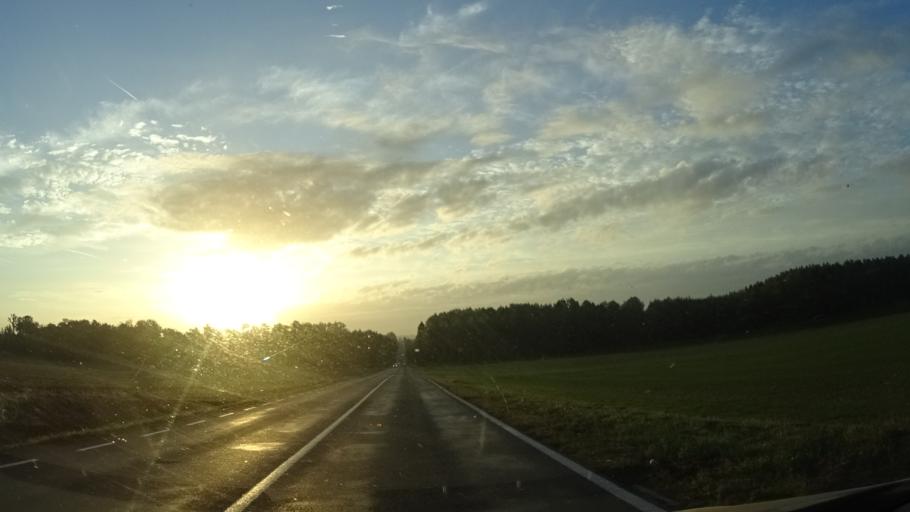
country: BE
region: Wallonia
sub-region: Province du Hainaut
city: Quevy-le-Petit
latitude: 50.3898
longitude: 3.9761
